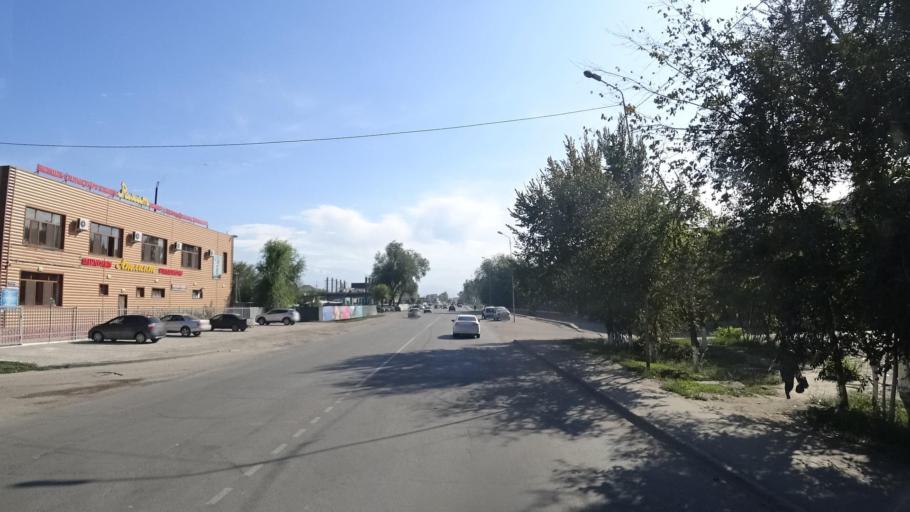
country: KZ
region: Almaty Oblysy
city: Energeticheskiy
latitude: 43.4238
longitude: 77.0240
